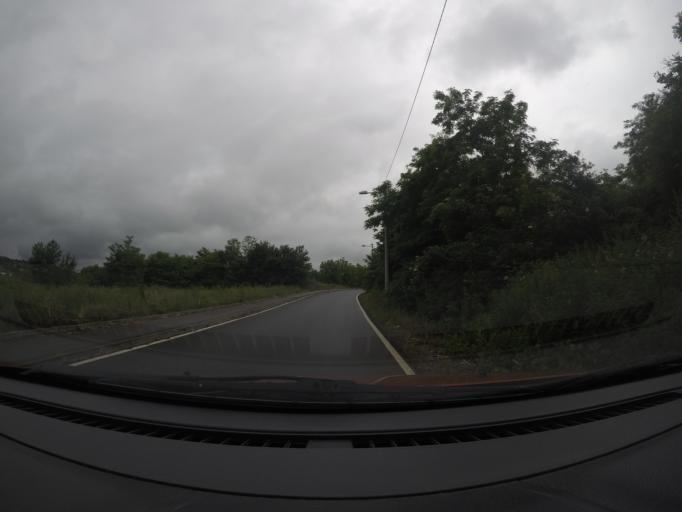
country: RS
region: Central Serbia
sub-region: Belgrade
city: Zvezdara
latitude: 44.7063
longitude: 20.5647
